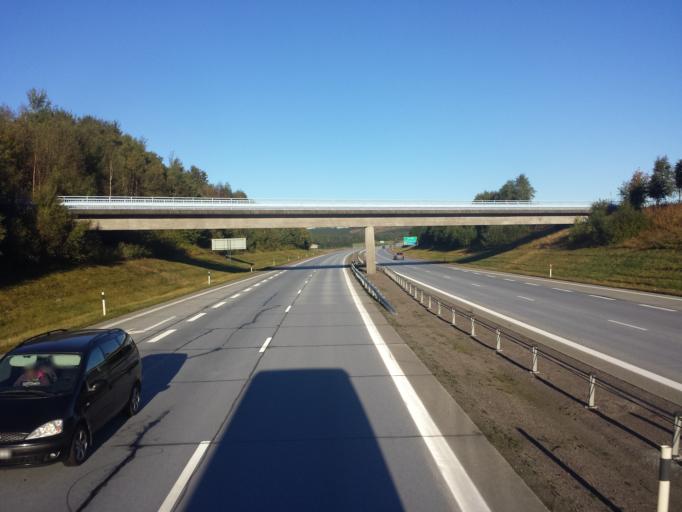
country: SE
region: Halland
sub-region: Halmstads Kommun
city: Getinge
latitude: 56.8076
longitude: 12.7331
